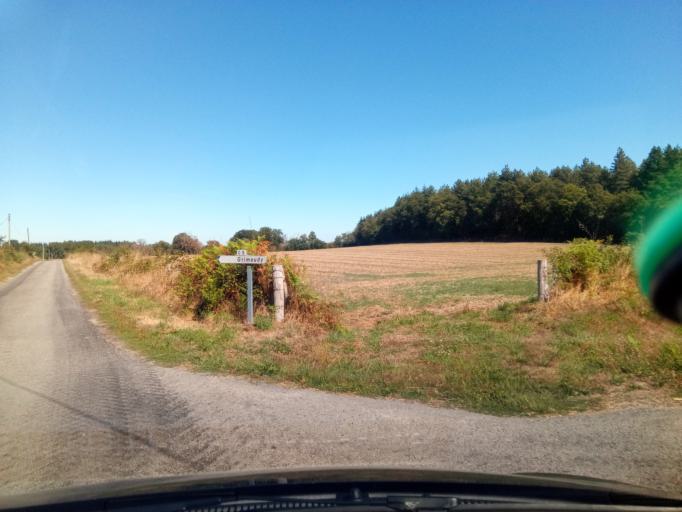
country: FR
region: Limousin
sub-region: Departement de la Haute-Vienne
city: Nantiat
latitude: 46.0806
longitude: 1.2103
